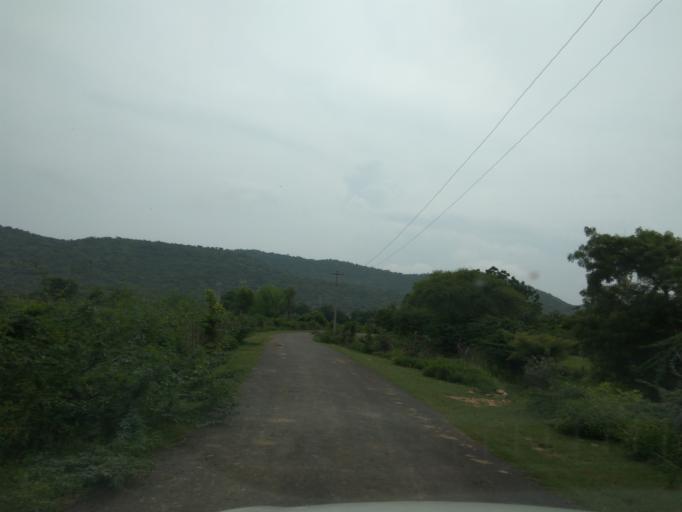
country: IN
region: Andhra Pradesh
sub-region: Prakasam
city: Cumbum
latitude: 15.4490
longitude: 79.0791
